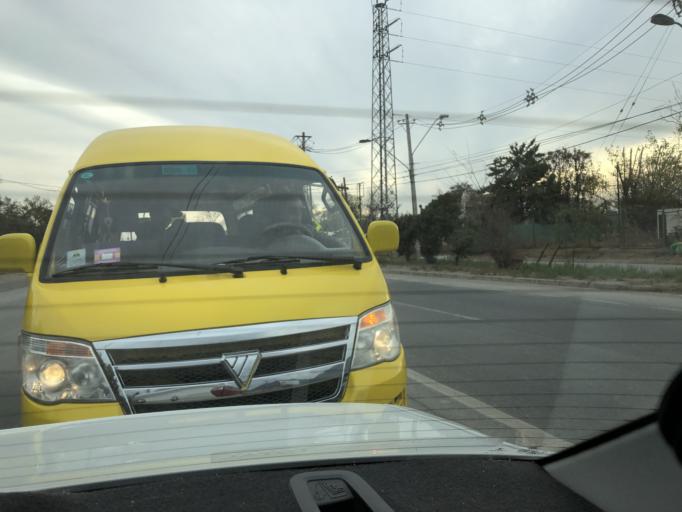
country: CL
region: Santiago Metropolitan
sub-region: Provincia de Cordillera
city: Puente Alto
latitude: -33.5979
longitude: -70.5121
